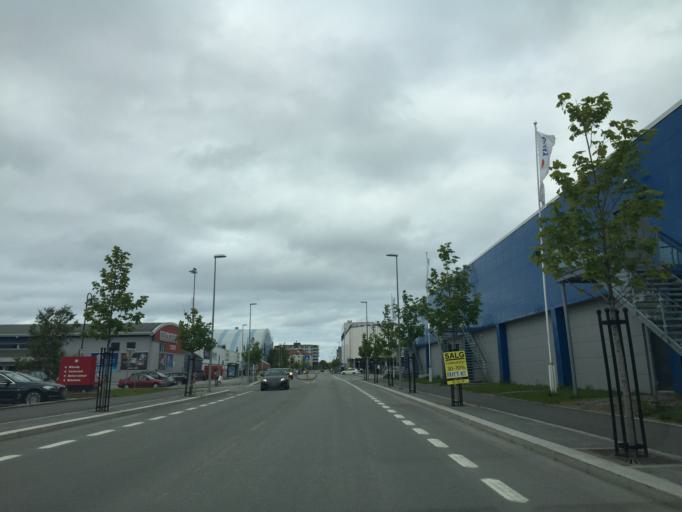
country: NO
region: Nordland
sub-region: Bodo
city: Bodo
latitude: 67.2762
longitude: 14.4217
